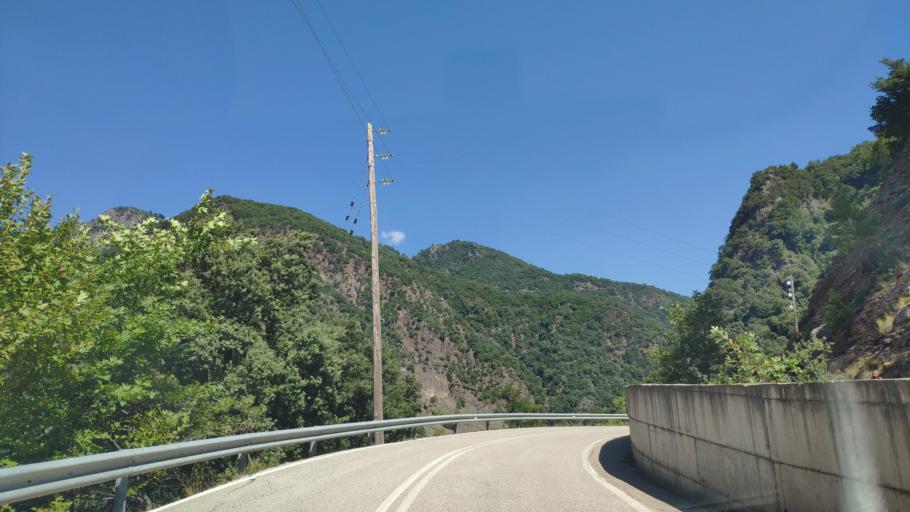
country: GR
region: Central Greece
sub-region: Nomos Evrytanias
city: Kerasochori
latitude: 39.0444
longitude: 21.5964
